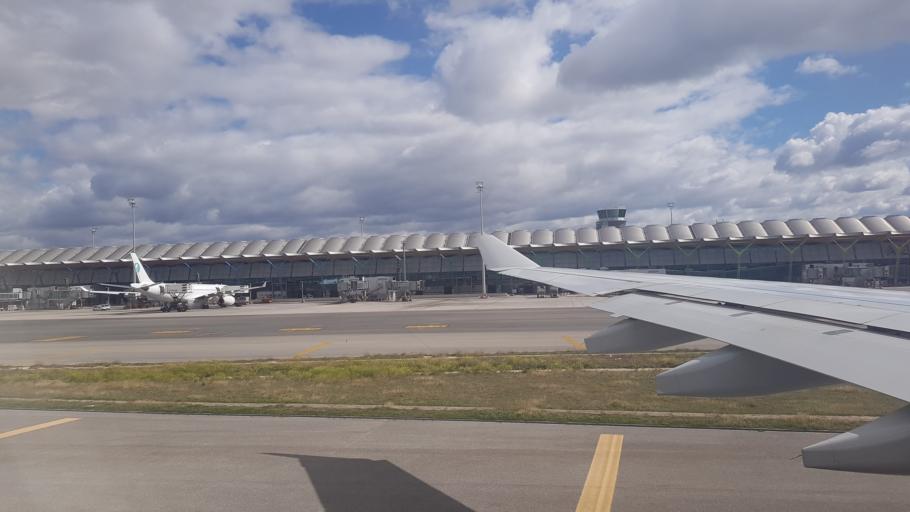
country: ES
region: Madrid
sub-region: Provincia de Madrid
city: Barajas de Madrid
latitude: 40.4964
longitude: -3.5712
